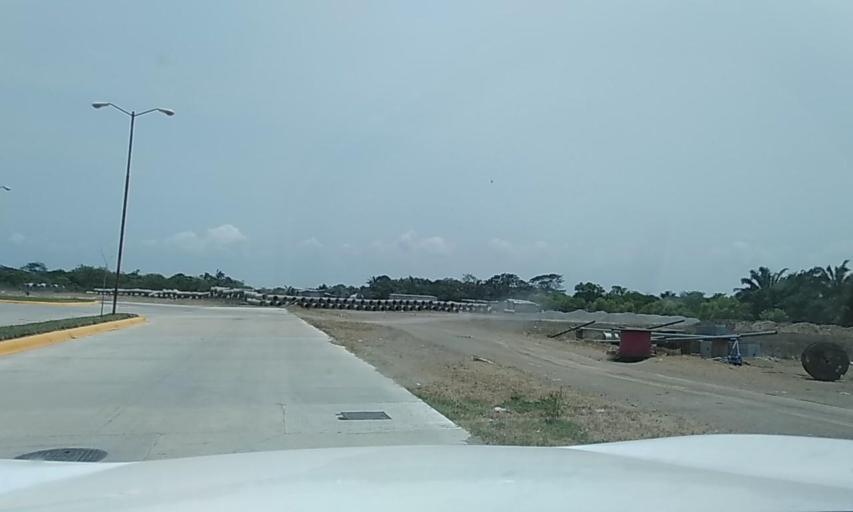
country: MX
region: Veracruz
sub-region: Veracruz
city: Hacienda Sotavento
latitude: 19.1225
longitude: -96.1714
